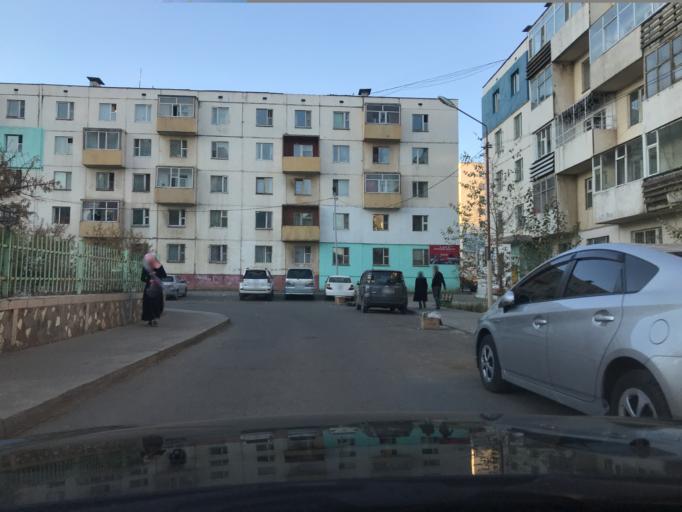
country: MN
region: Ulaanbaatar
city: Ulaanbaatar
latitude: 47.9255
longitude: 106.9055
